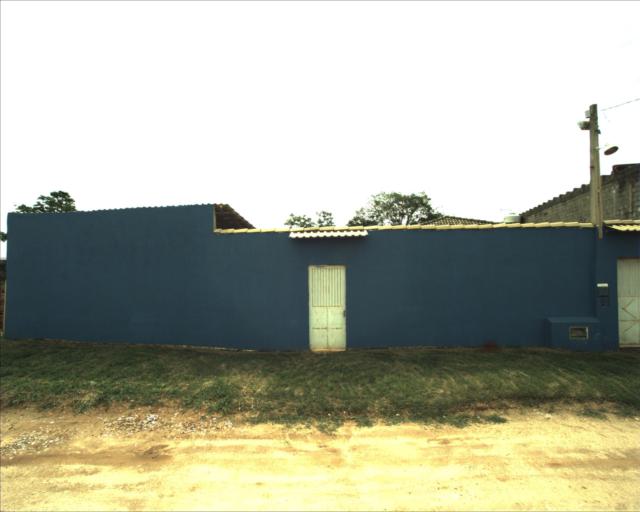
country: BR
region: Sao Paulo
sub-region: Aracoiaba Da Serra
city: Aracoiaba da Serra
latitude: -23.5599
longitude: -47.5562
